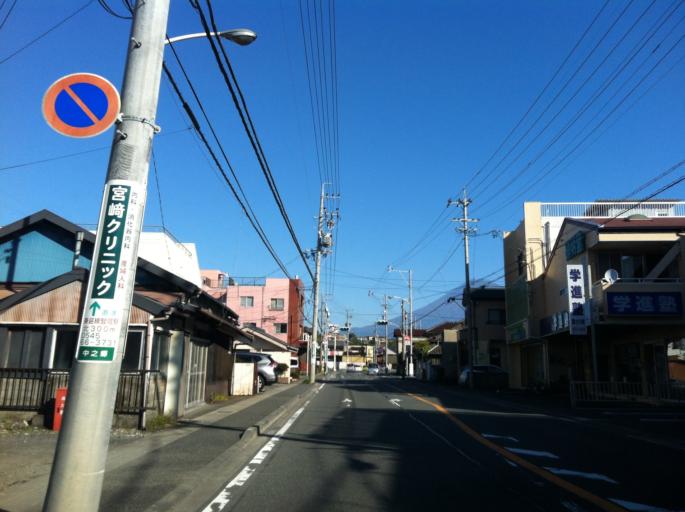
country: JP
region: Shizuoka
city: Fuji
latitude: 35.1423
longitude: 138.6179
